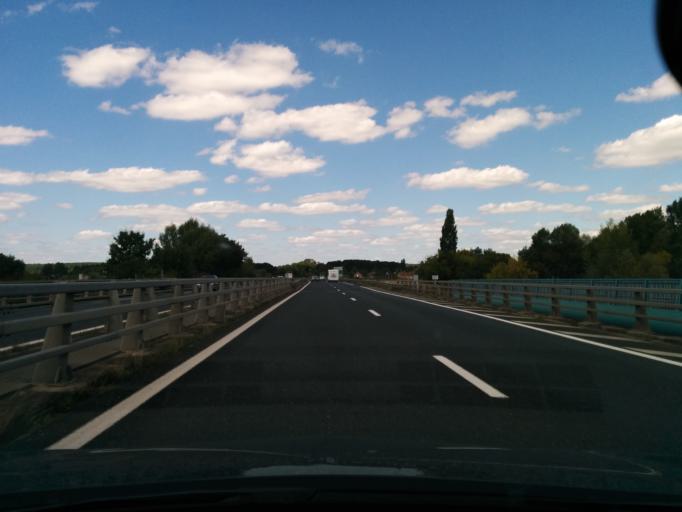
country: FR
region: Centre
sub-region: Departement du Cher
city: Vierzon
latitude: 47.2177
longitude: 2.0404
